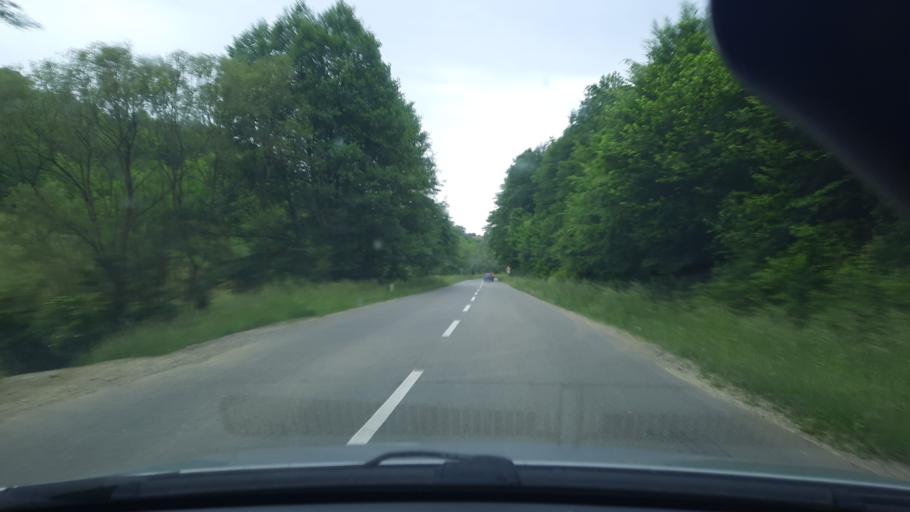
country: RS
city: Bukor
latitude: 44.5072
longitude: 19.4977
